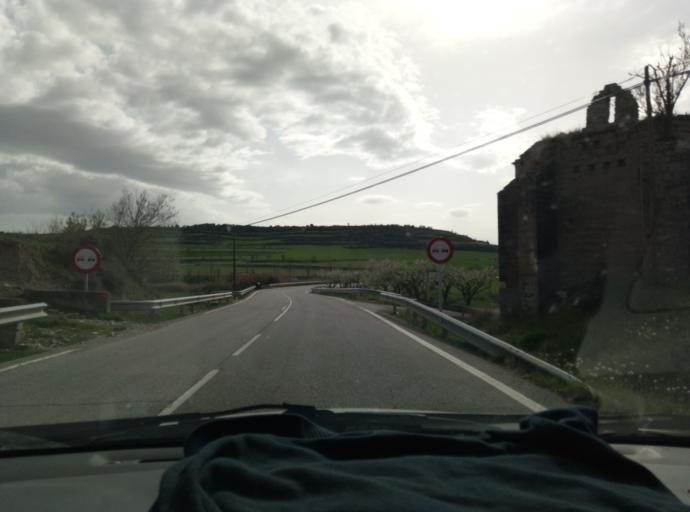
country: ES
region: Catalonia
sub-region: Provincia de Lleida
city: Cervera
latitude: 41.6638
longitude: 1.2625
